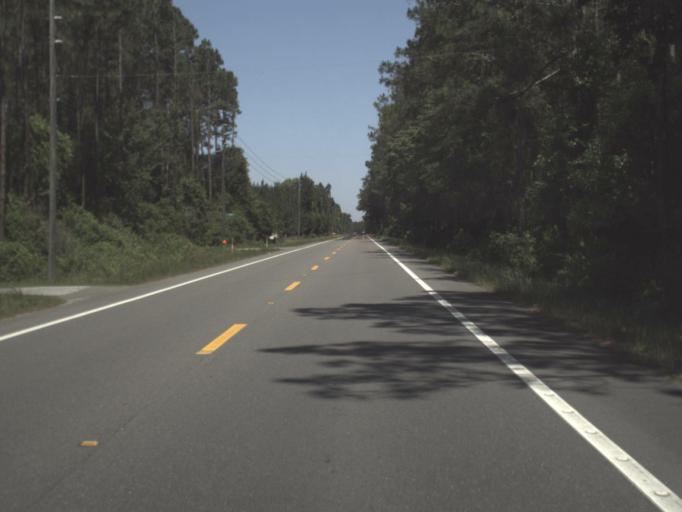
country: US
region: Florida
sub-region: Baker County
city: Macclenny
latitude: 30.2916
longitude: -82.0635
